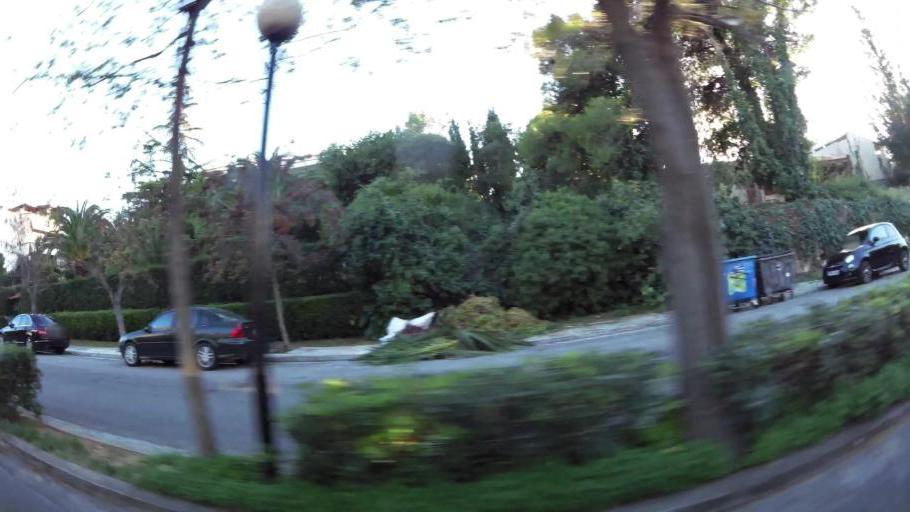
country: GR
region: Attica
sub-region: Nomarchia Athinas
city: Nea Erythraia
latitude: 38.0874
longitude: 23.8222
